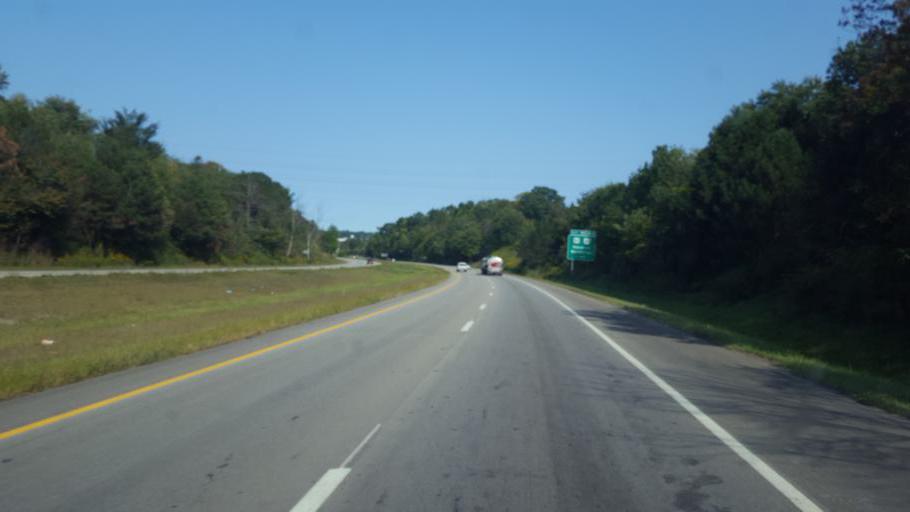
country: US
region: Ohio
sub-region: Stark County
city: Navarre
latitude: 40.7561
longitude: -81.5400
